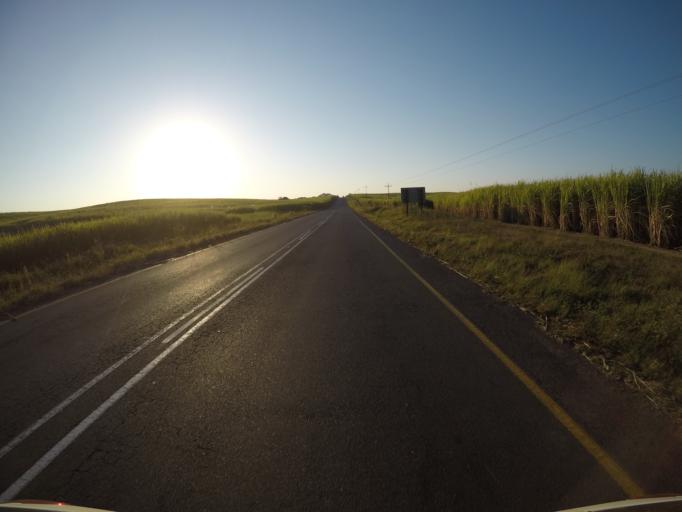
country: ZA
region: KwaZulu-Natal
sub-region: uThungulu District Municipality
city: eSikhawini
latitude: -28.9482
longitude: 31.7274
